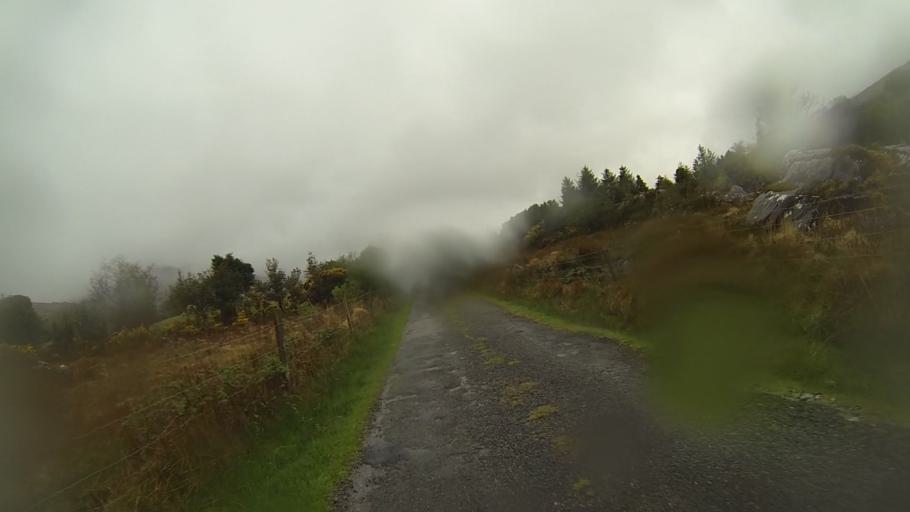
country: IE
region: Munster
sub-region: Ciarrai
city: Kenmare
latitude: 51.9488
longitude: -9.6687
